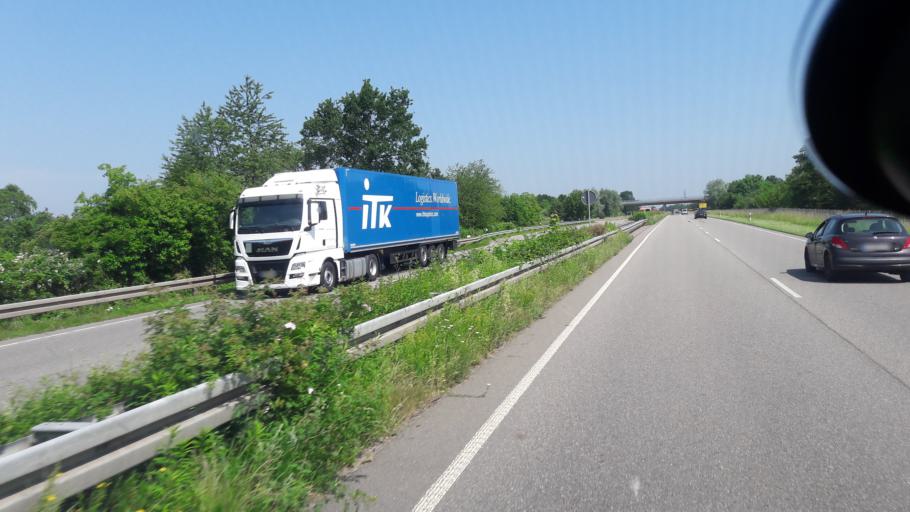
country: DE
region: Baden-Wuerttemberg
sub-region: Karlsruhe Region
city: Bischweier
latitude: 48.8375
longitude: 8.2679
